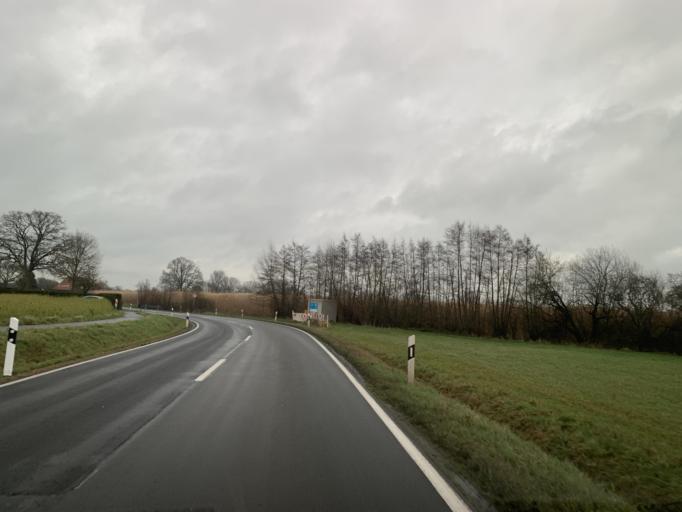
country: DE
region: North Rhine-Westphalia
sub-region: Regierungsbezirk Munster
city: Nordwalde
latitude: 52.1046
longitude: 7.4810
